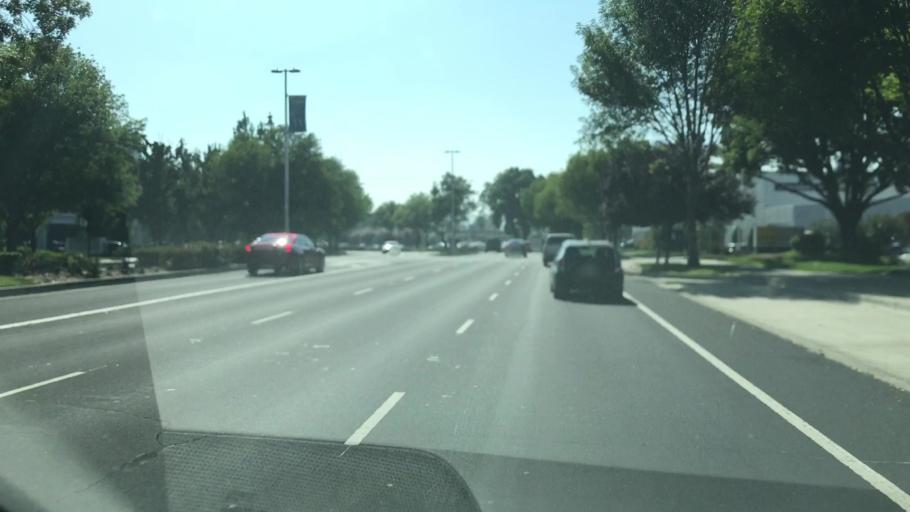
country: US
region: California
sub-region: Alameda County
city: Dublin
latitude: 37.7000
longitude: -121.9003
